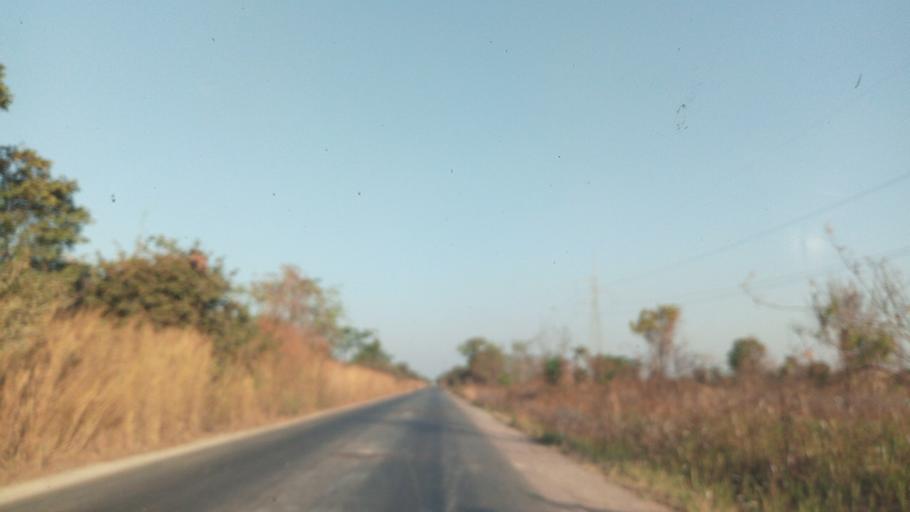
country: CD
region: Katanga
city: Likasi
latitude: -11.1122
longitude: 27.0238
